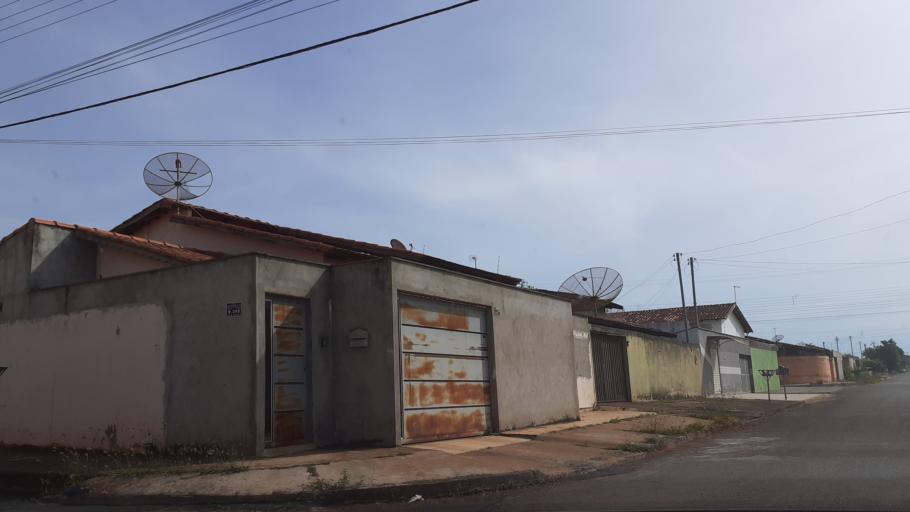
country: BR
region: Goias
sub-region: Itumbiara
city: Itumbiara
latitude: -18.4235
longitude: -49.2434
